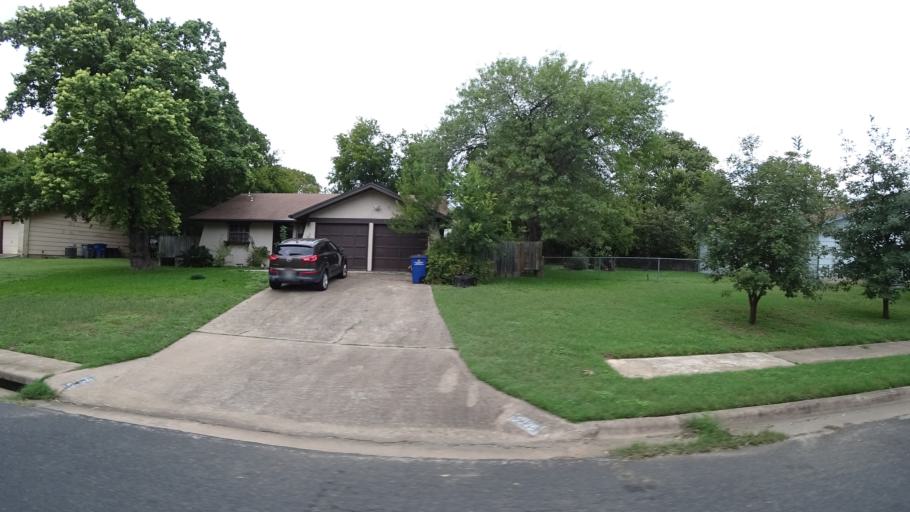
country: US
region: Texas
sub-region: Travis County
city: Rollingwood
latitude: 30.2155
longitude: -97.7863
